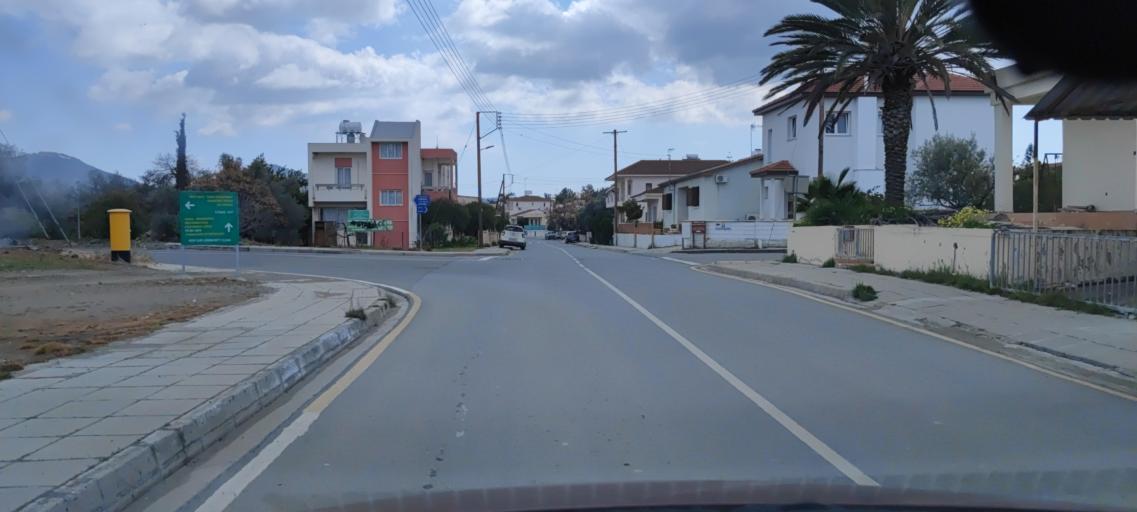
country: CY
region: Larnaka
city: Kornos
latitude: 34.9171
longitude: 33.4013
